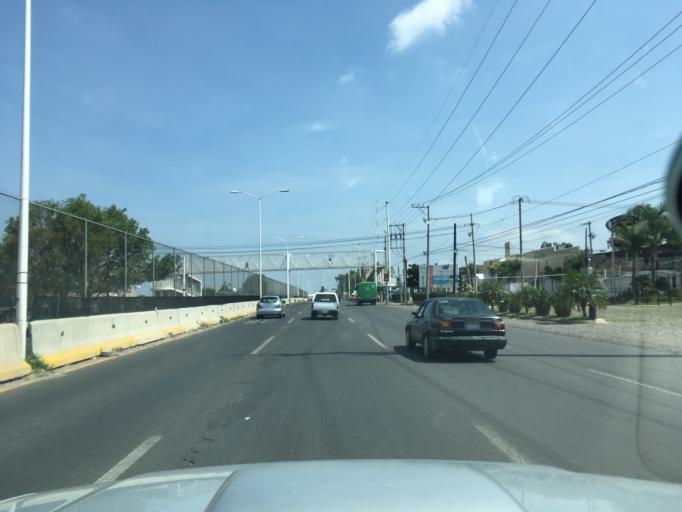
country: MX
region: Jalisco
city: Tonala
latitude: 20.6711
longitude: -103.2358
